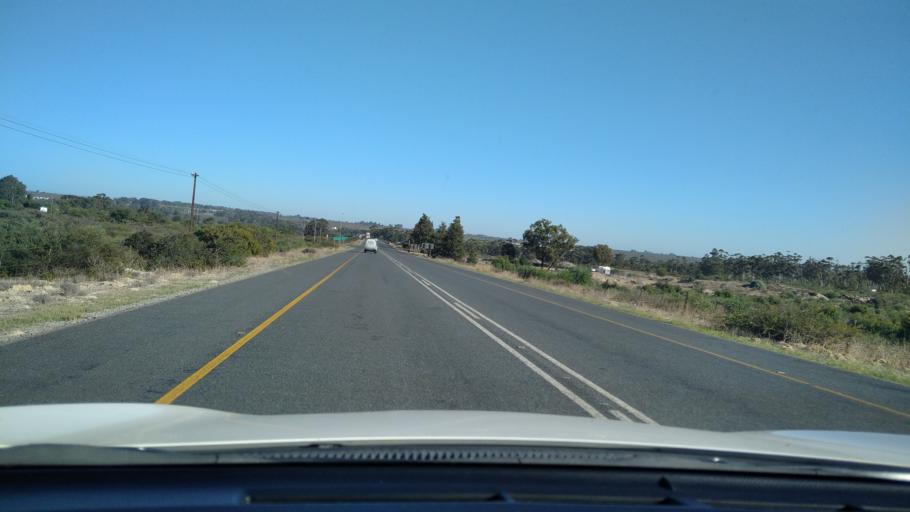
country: ZA
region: Western Cape
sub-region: West Coast District Municipality
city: Moorreesburg
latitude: -33.0644
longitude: 18.3605
